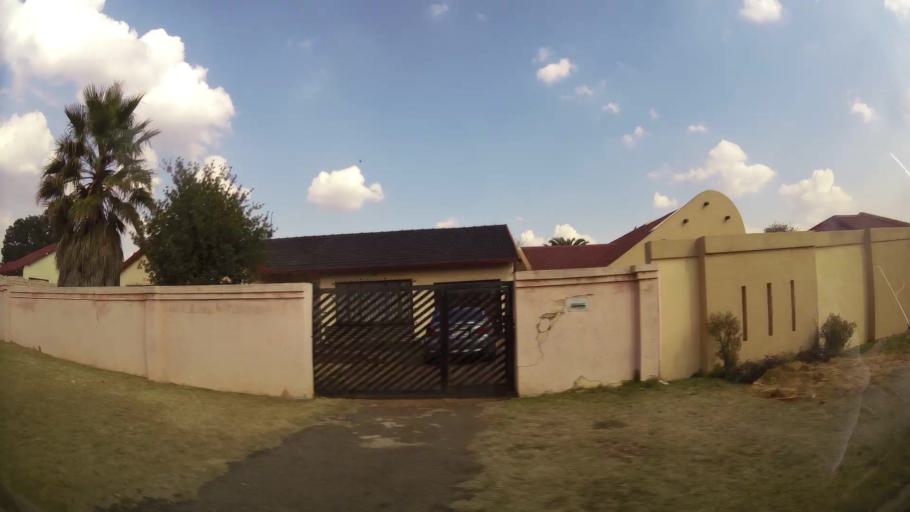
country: ZA
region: Gauteng
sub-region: Ekurhuleni Metropolitan Municipality
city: Germiston
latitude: -26.3085
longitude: 28.1848
